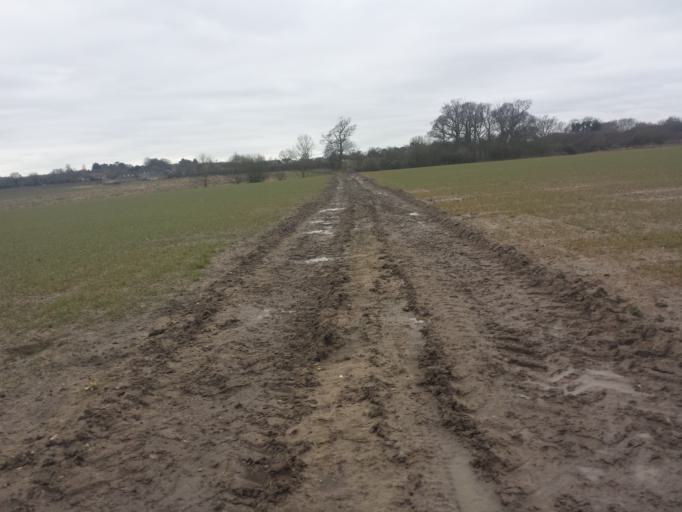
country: GB
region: England
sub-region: Essex
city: Little Clacton
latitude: 51.8850
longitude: 1.1742
